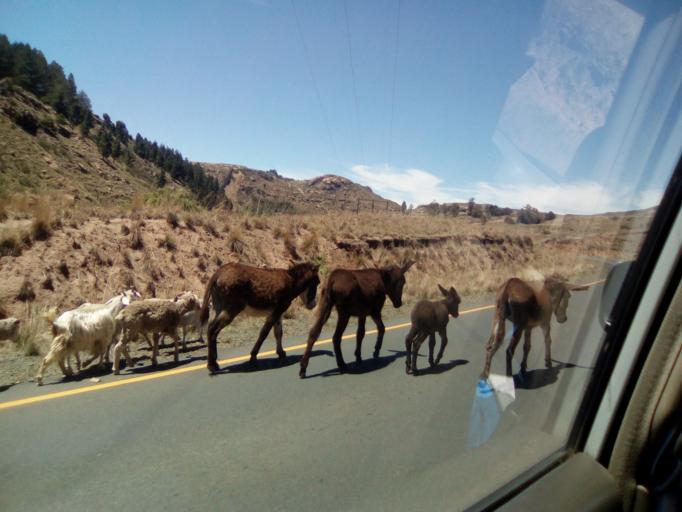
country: LS
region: Qacha's Nek
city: Qacha's Nek
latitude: -30.1038
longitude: 28.6564
